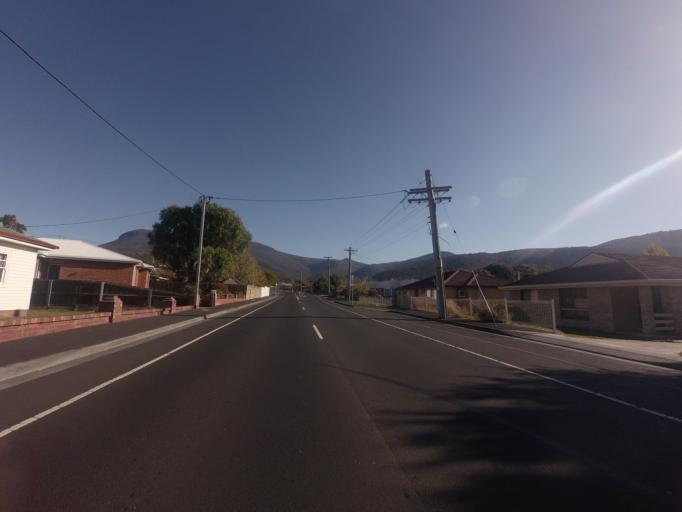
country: AU
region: Tasmania
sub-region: Glenorchy
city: Glenorchy
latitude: -42.8432
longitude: 147.2675
